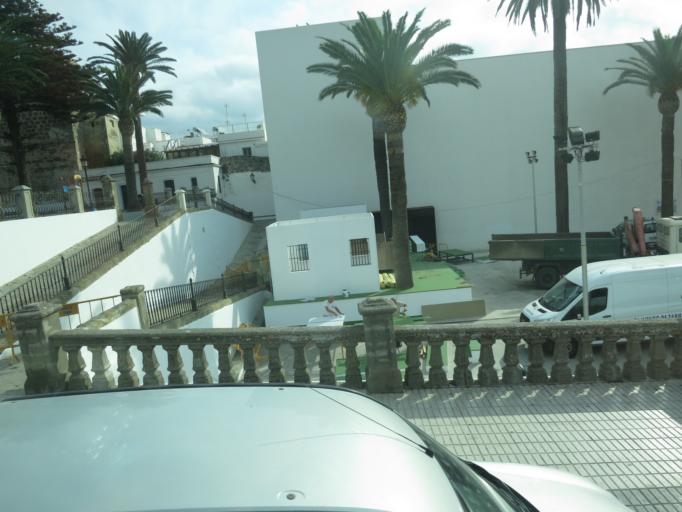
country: ES
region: Andalusia
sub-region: Provincia de Cadiz
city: Tarifa
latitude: 36.0132
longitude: -5.6054
